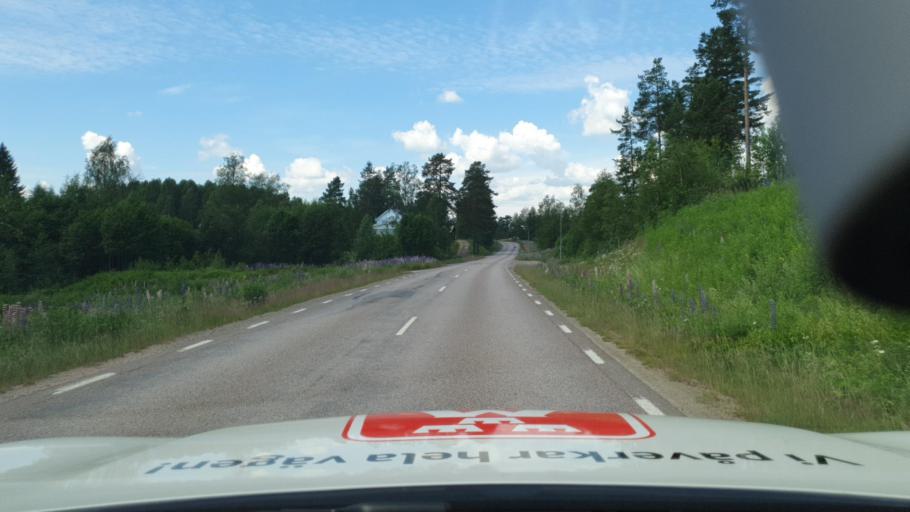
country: SE
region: Vaermland
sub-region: Torsby Kommun
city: Torsby
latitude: 60.3370
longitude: 12.9971
